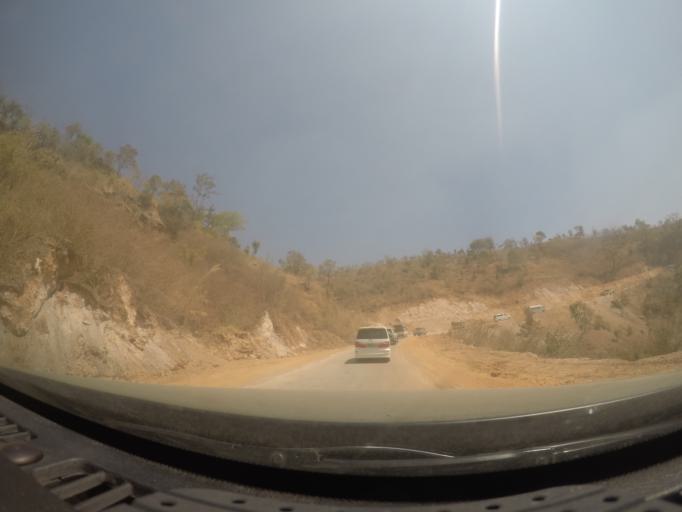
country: MM
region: Shan
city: Taunggyi
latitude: 20.8093
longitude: 97.2766
